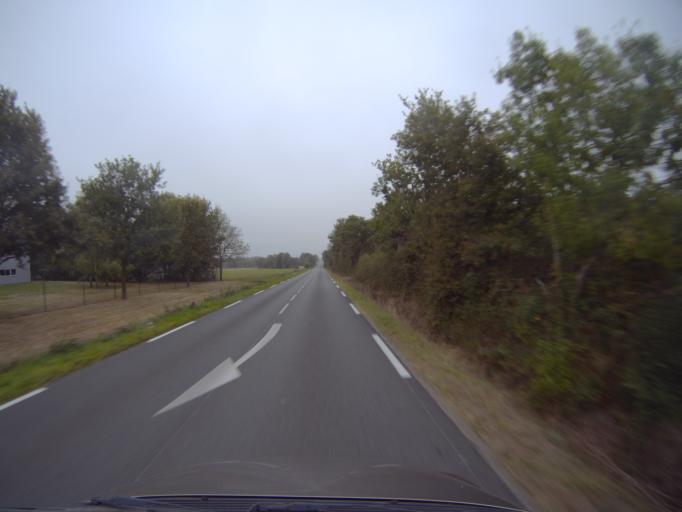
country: FR
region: Pays de la Loire
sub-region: Departement de la Vendee
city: La Bernardiere
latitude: 47.0253
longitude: -1.2671
